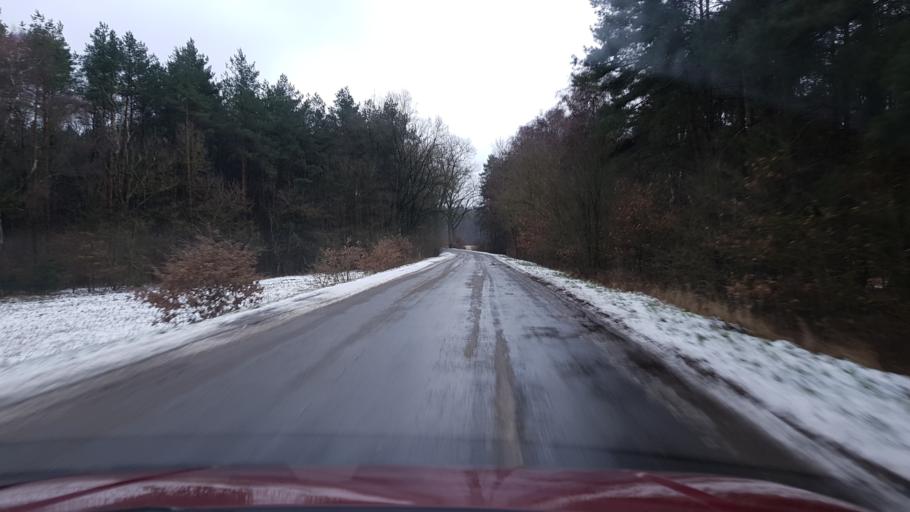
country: PL
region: West Pomeranian Voivodeship
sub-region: Powiat goleniowski
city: Nowogard
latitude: 53.6401
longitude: 15.1218
